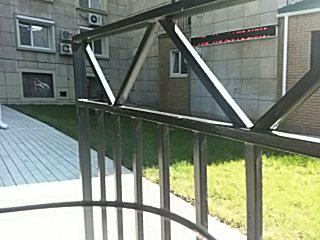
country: RU
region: Tatarstan
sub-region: Tukayevskiy Rayon
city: Naberezhnyye Chelny
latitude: 55.7461
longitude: 52.4162
